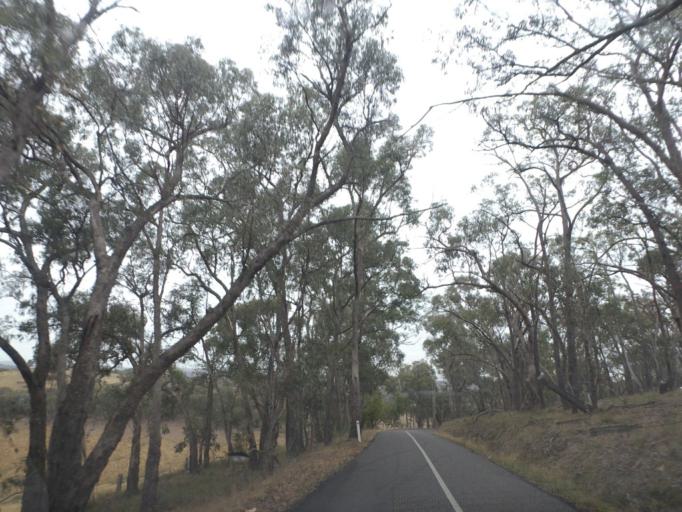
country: AU
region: Victoria
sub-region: Nillumbik
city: Saint Andrews
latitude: -37.6347
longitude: 145.2806
